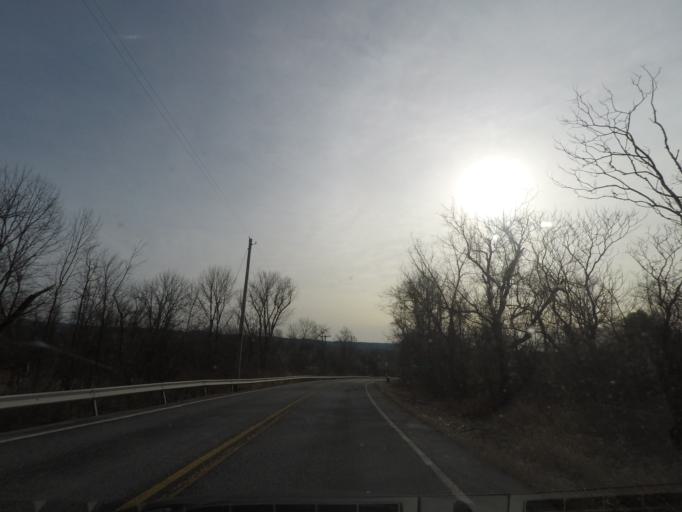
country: US
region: New York
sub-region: Saratoga County
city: Stillwater
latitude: 42.9755
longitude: -73.6341
